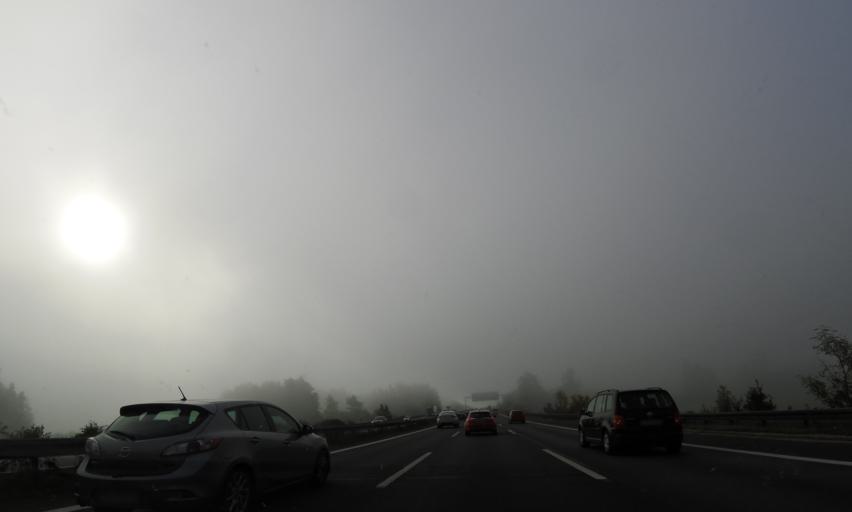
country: DE
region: Bavaria
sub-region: Regierungsbezirk Mittelfranken
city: Velden
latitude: 49.6758
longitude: 11.4680
